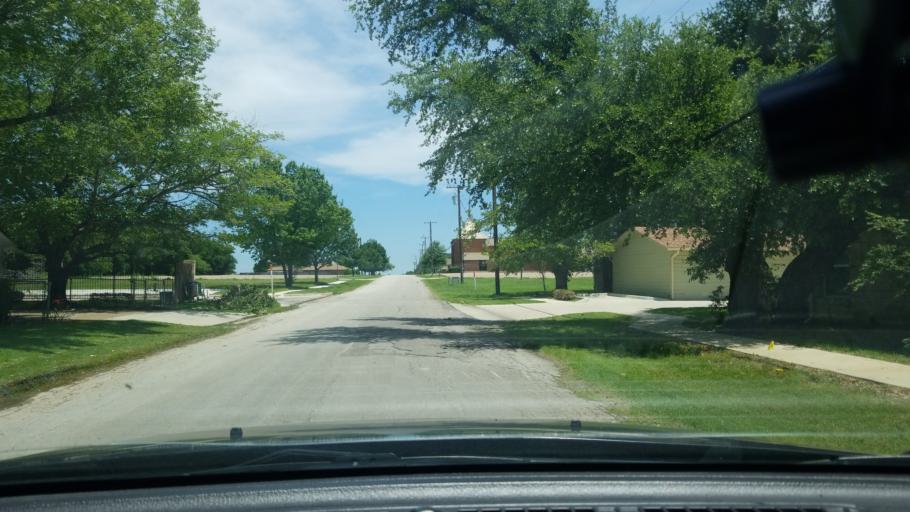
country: US
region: Texas
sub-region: Dallas County
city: Mesquite
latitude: 32.7808
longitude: -96.6003
